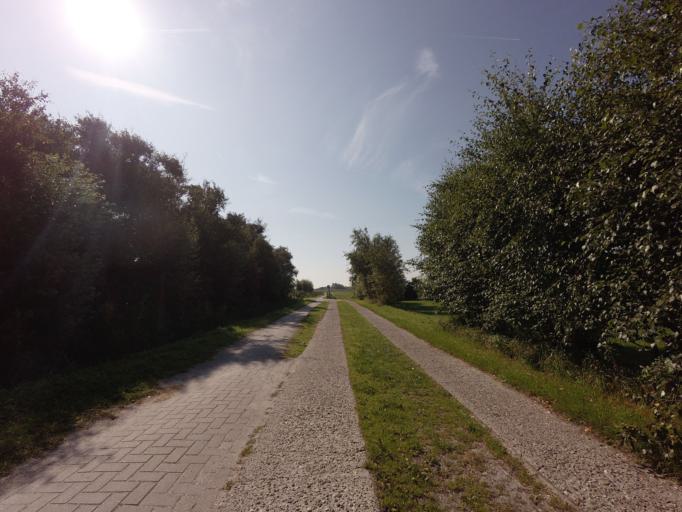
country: NL
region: Friesland
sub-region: Gemeente Schiermonnikoog
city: Schiermonnikoog
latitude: 53.4761
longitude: 6.1547
